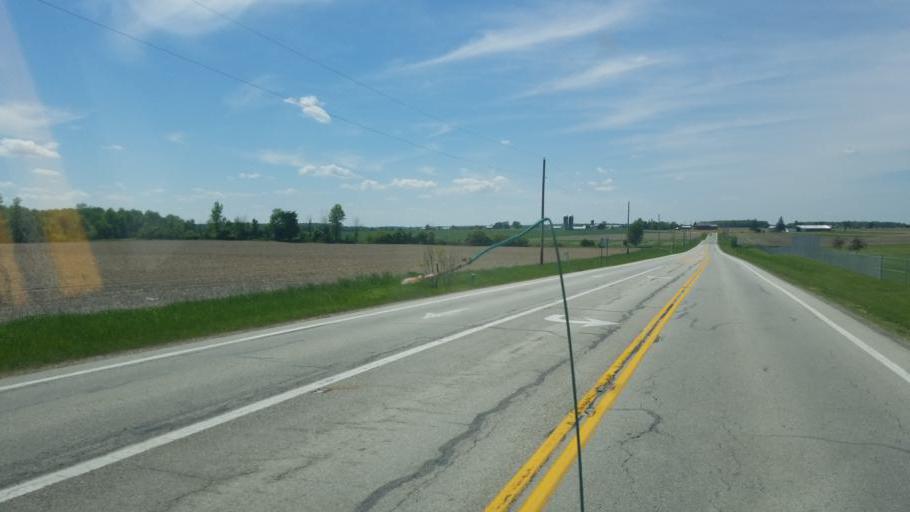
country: US
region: Ohio
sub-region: Huron County
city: Willard
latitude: 41.0771
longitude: -82.9188
